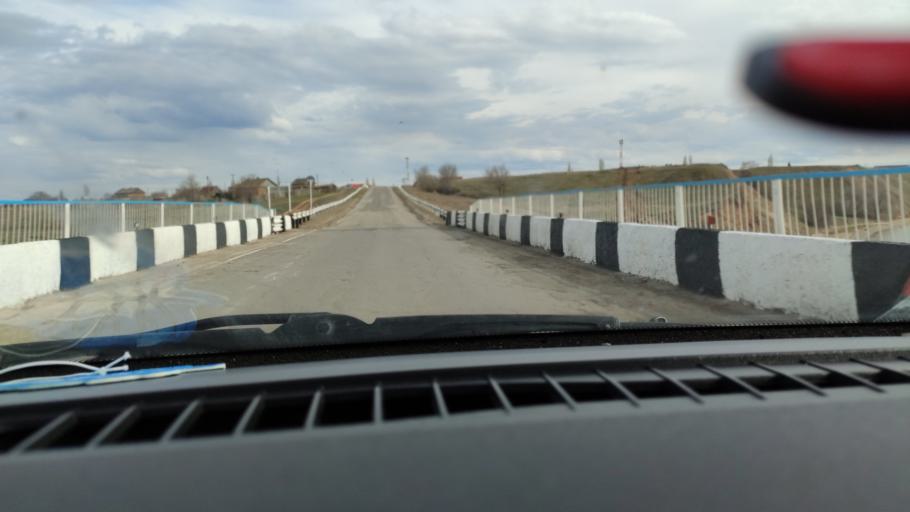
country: RU
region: Saratov
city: Rovnoye
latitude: 51.0266
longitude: 46.0922
